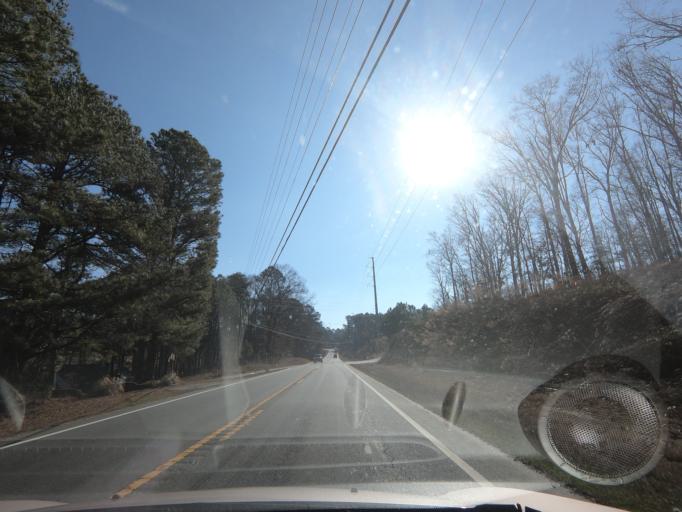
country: US
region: Georgia
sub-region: Forsyth County
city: Cumming
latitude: 34.3038
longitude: -84.2013
